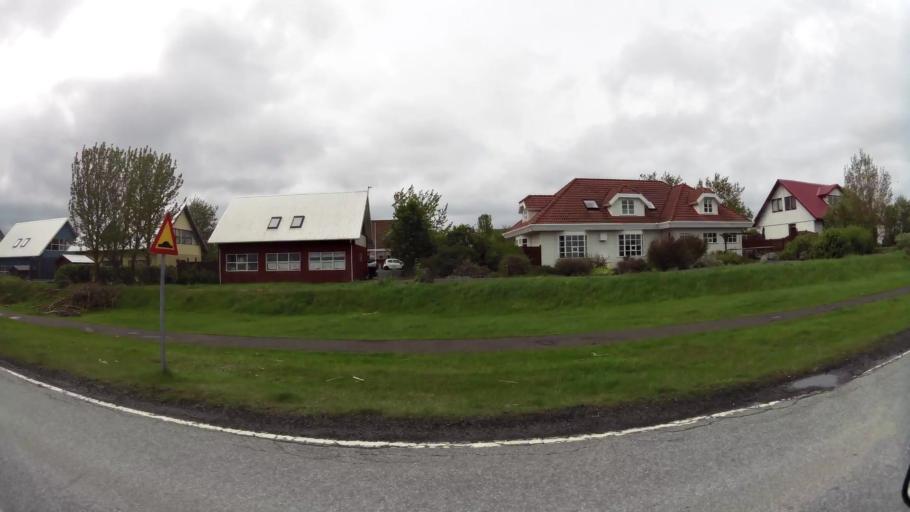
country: IS
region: Capital Region
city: Alftanes
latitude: 64.1073
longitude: -22.0098
